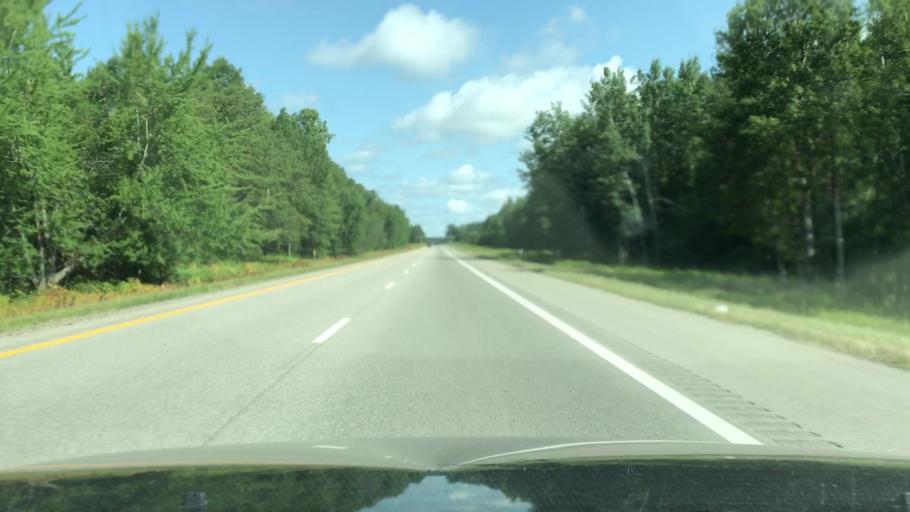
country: US
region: Michigan
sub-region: Montcalm County
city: Howard City
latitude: 43.5178
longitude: -85.4860
